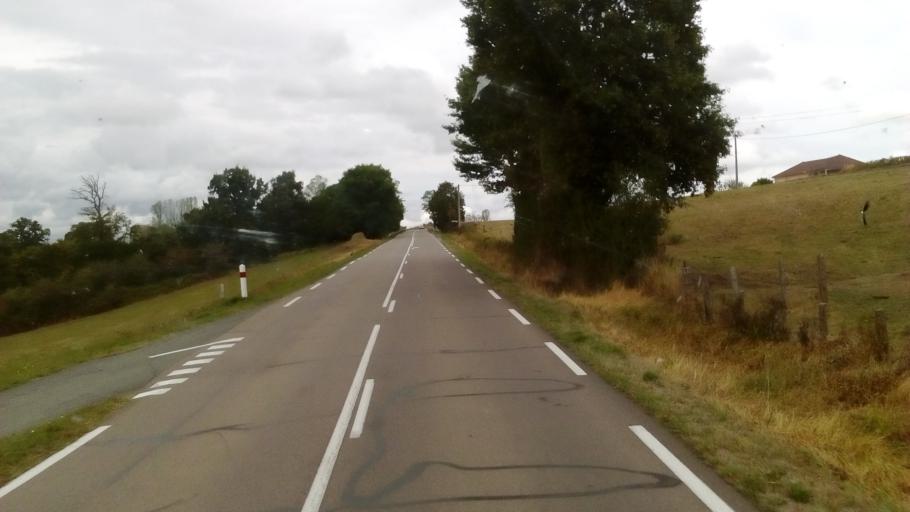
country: FR
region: Bourgogne
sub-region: Departement de Saone-et-Loire
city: Saint-Yan
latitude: 46.4424
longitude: 4.0176
